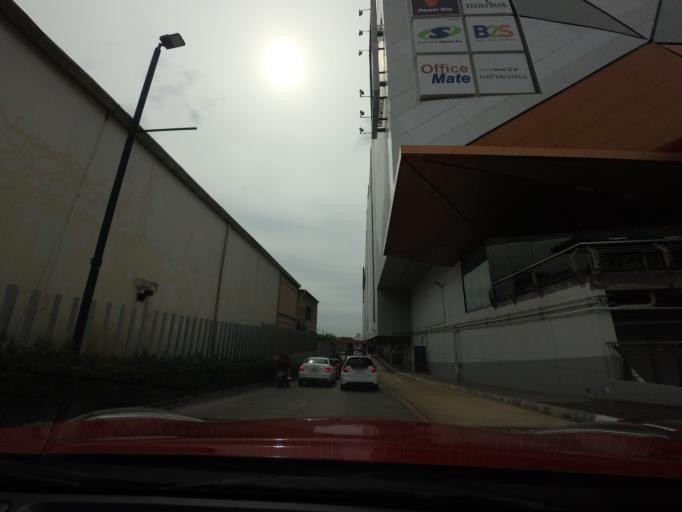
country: TH
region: Songkhla
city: Hat Yai
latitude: 6.9907
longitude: 100.4840
